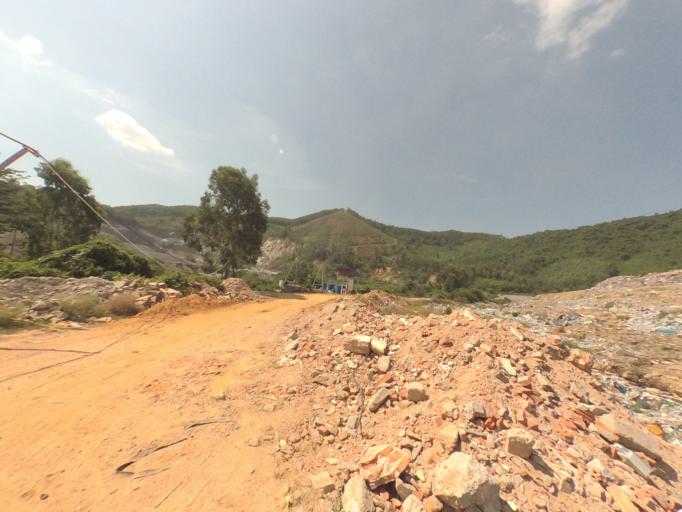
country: VN
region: Da Nang
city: Lien Chieu
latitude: 16.0416
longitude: 108.1437
